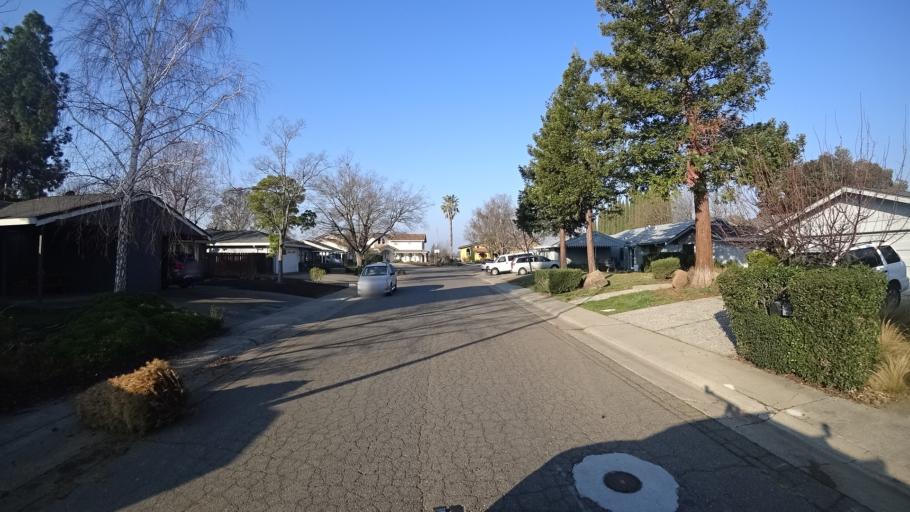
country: US
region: California
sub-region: Yolo County
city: Davis
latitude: 38.5568
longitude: -121.7926
